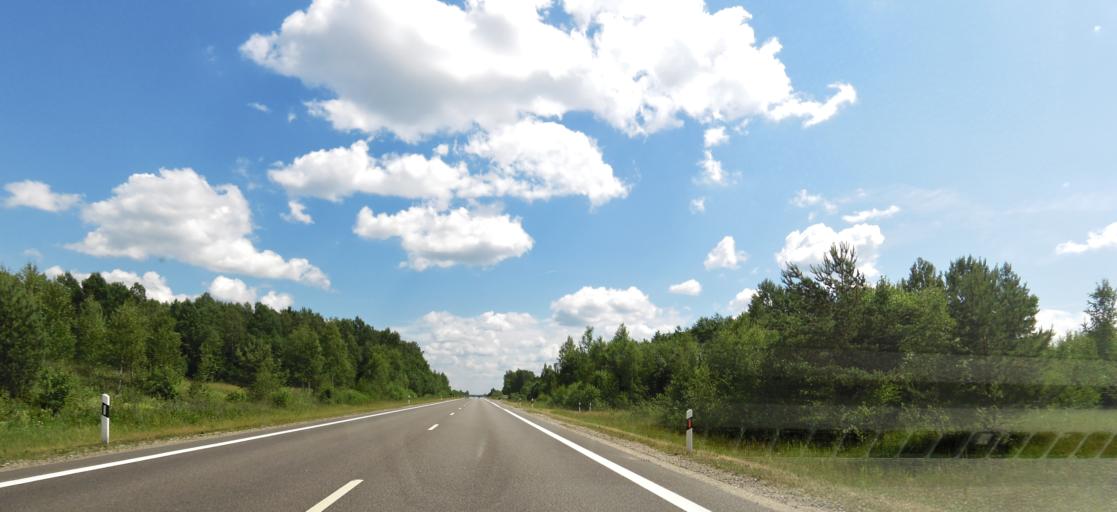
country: LT
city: Skaidiskes
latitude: 54.5716
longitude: 25.6200
